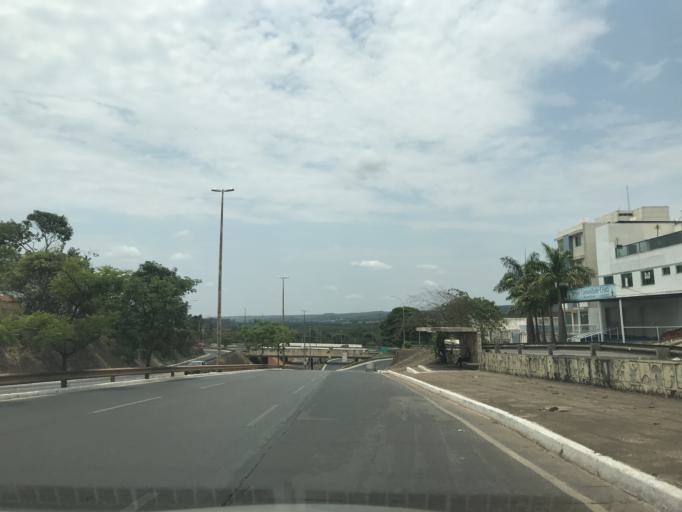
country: BR
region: Federal District
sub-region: Brasilia
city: Brasilia
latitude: -15.6624
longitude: -47.8058
